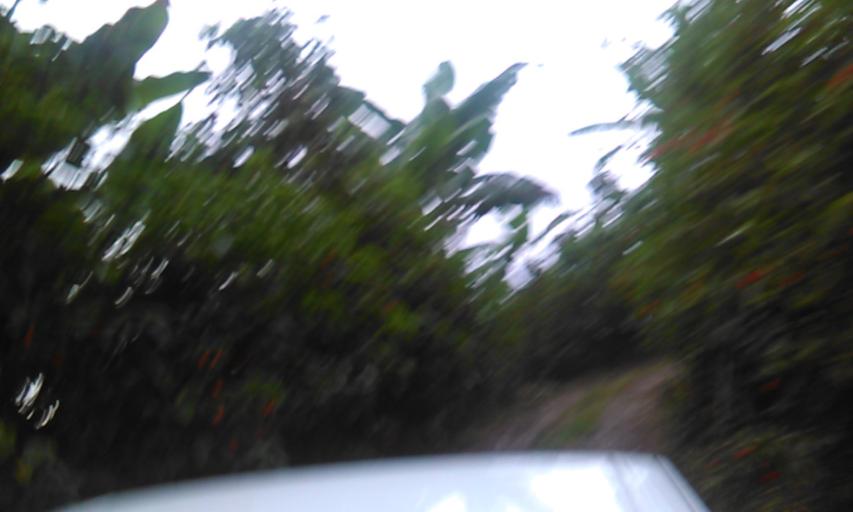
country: CO
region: Quindio
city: Cordoba
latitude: 4.4096
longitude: -75.6838
